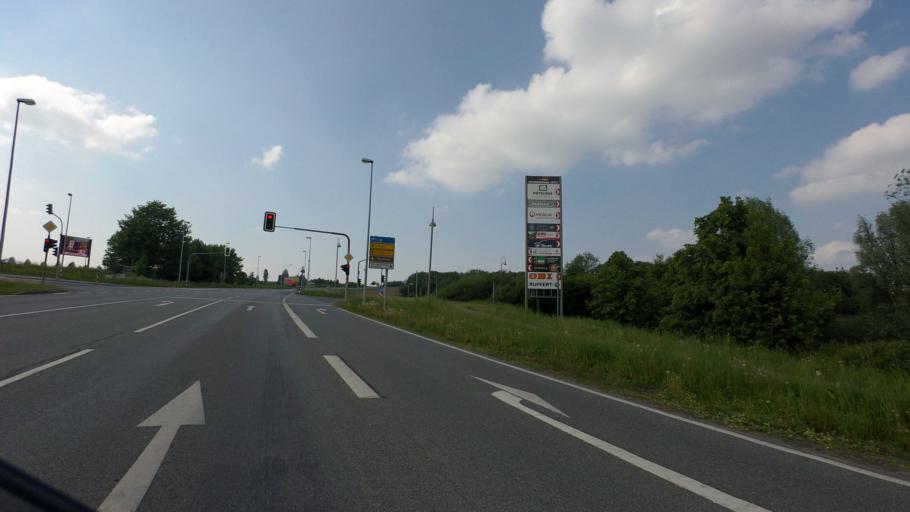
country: DE
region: Saxony
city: Lobau
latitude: 51.1058
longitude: 14.6541
